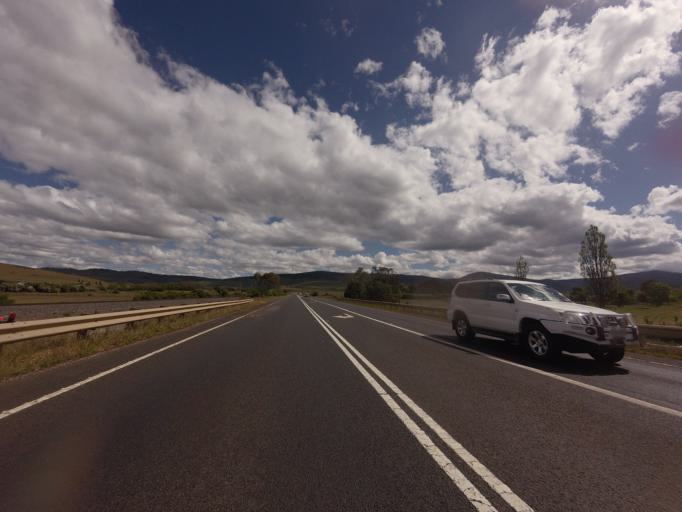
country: AU
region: Tasmania
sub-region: Brighton
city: Bridgewater
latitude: -42.1756
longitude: 147.3896
